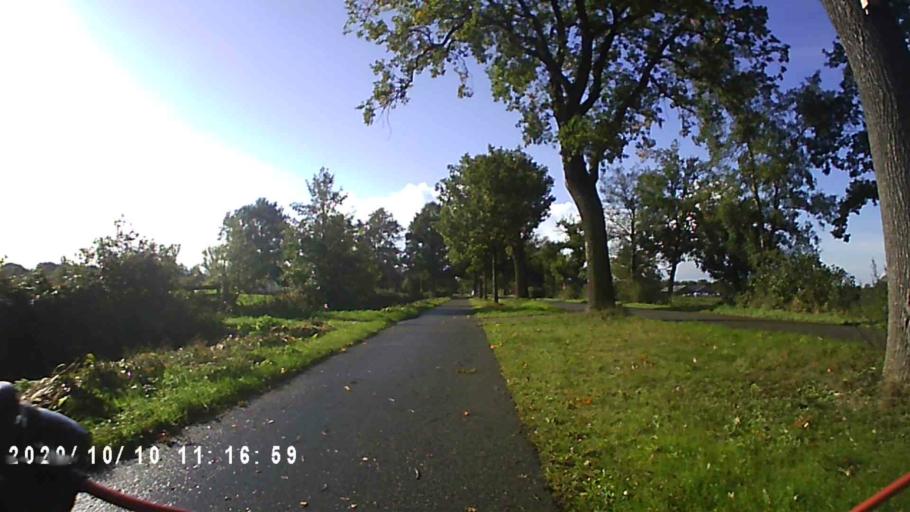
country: NL
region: Friesland
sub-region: Gemeente Smallingerland
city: Drachtstercompagnie
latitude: 53.0980
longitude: 6.1989
